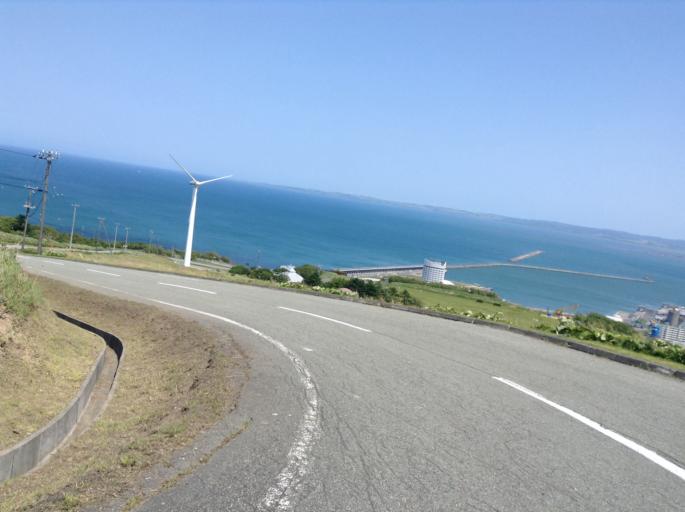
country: JP
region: Hokkaido
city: Wakkanai
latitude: 45.4172
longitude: 141.6660
